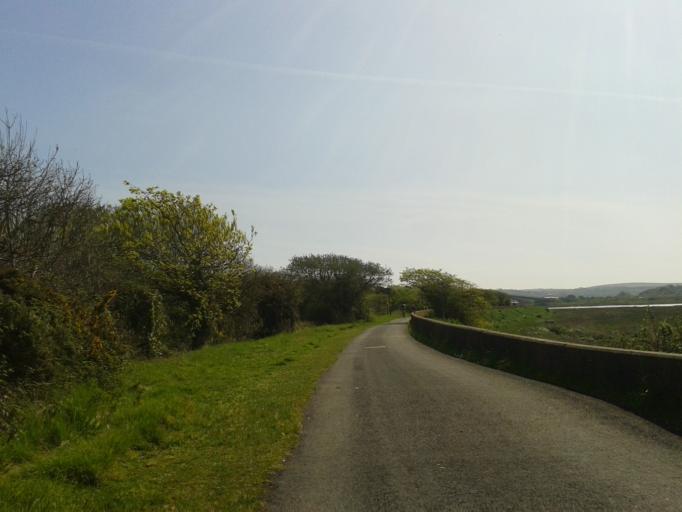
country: GB
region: England
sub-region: Devon
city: Barnstaple
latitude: 51.0829
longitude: -4.0786
